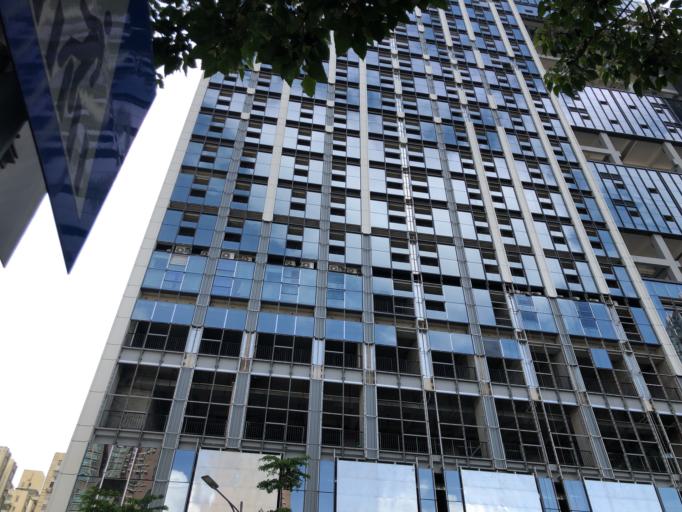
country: CN
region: Guangdong
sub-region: Shenzhen
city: Shenzhen
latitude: 22.5403
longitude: 114.1106
